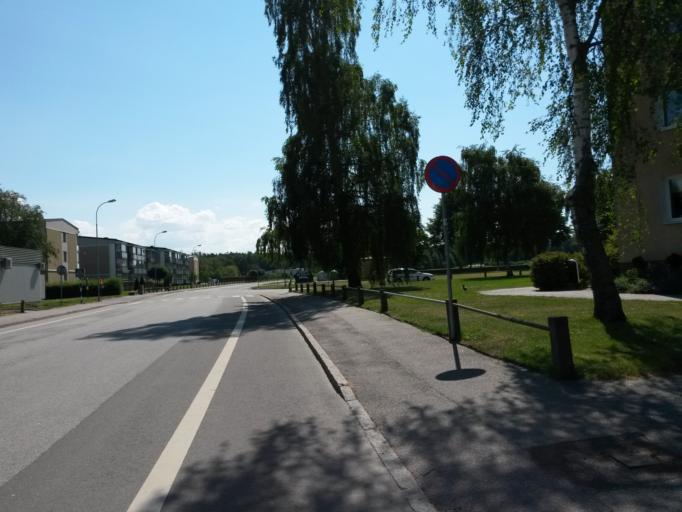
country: SE
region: Vaestra Goetaland
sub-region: Lidkopings Kommun
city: Lidkoping
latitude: 58.4927
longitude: 13.1560
